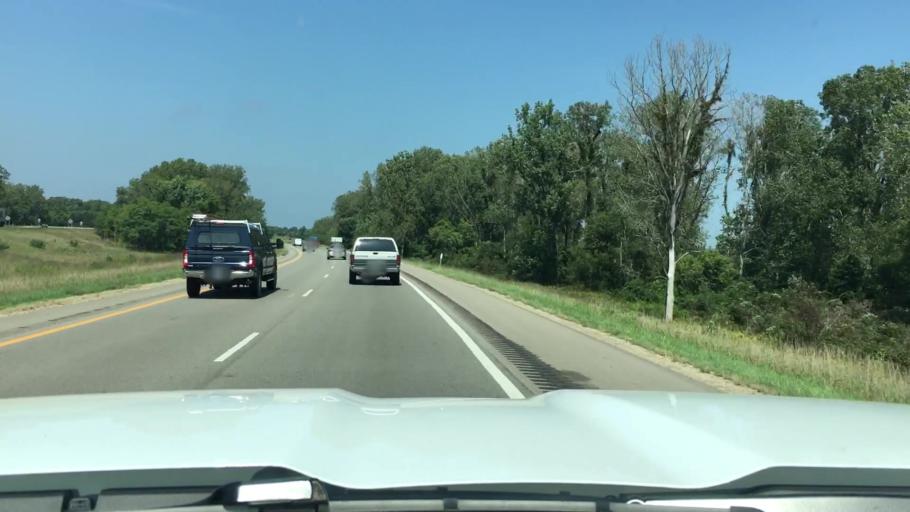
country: US
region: Michigan
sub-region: Kalamazoo County
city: Schoolcraft
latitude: 42.1479
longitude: -85.6385
